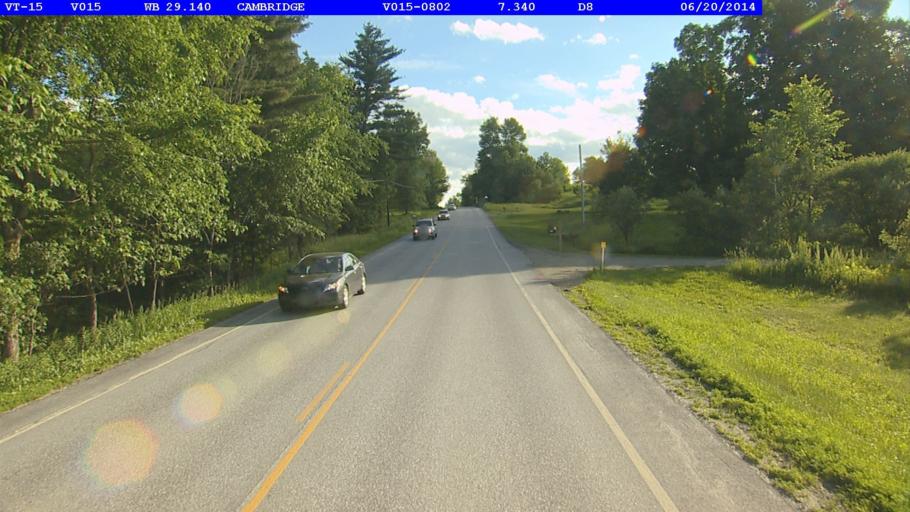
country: US
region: Vermont
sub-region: Lamoille County
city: Johnson
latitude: 44.6614
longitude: -72.7917
